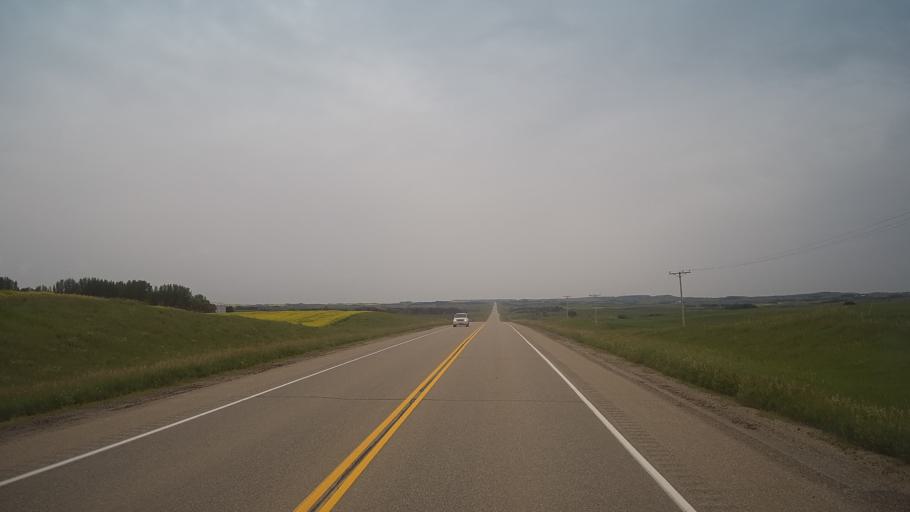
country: CA
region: Saskatchewan
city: Biggar
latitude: 52.0565
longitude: -107.7944
